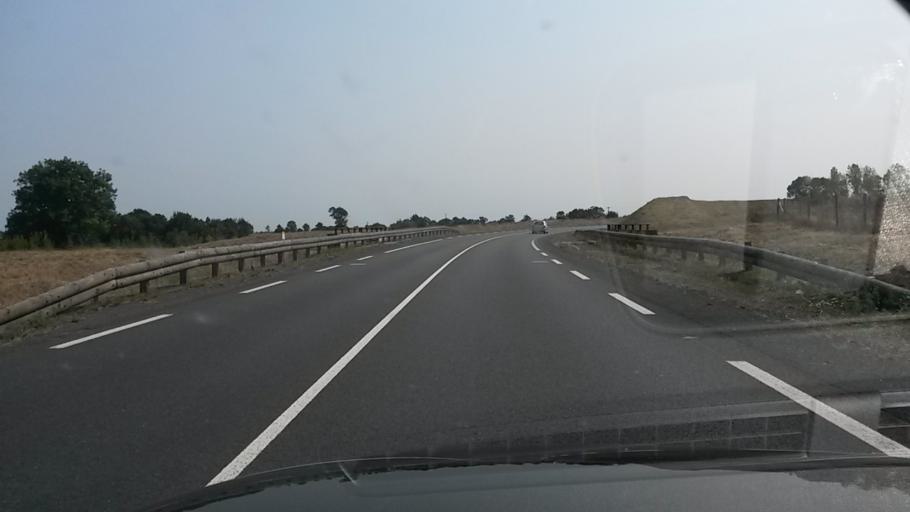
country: FR
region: Pays de la Loire
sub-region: Departement de la Loire-Atlantique
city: Mesanger
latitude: 47.4210
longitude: -1.1852
